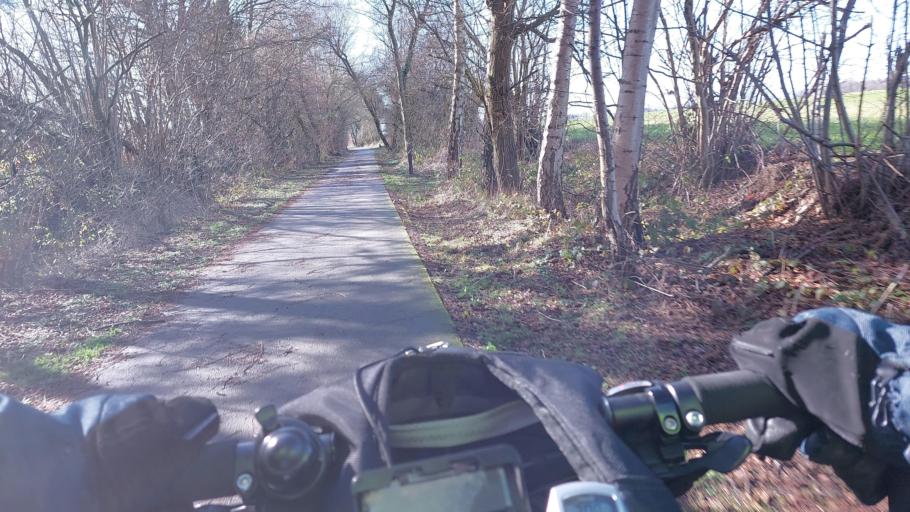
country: BE
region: Wallonia
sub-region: Province du Brabant Wallon
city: Nivelles
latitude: 50.5909
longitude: 4.2931
